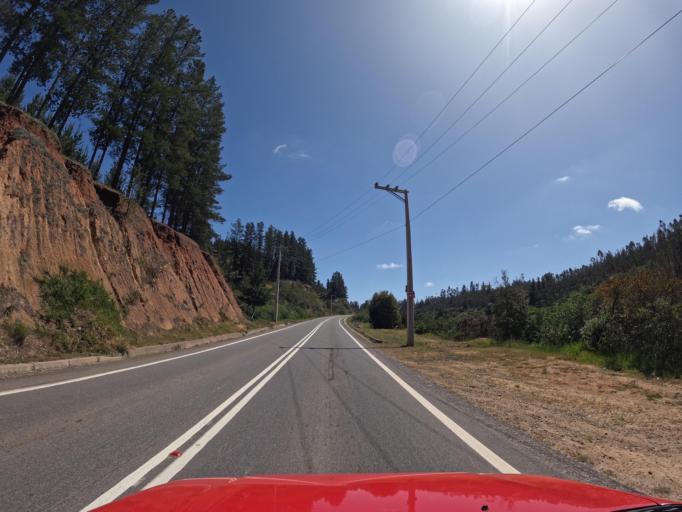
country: CL
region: O'Higgins
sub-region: Provincia de Colchagua
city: Santa Cruz
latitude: -34.6851
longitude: -71.7869
